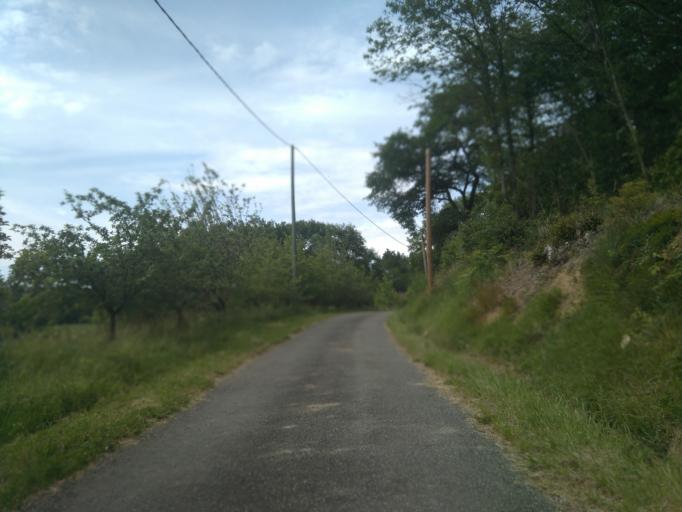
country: FR
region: Aquitaine
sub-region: Departement des Pyrenees-Atlantiques
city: Orthez
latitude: 43.4612
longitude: -0.7706
